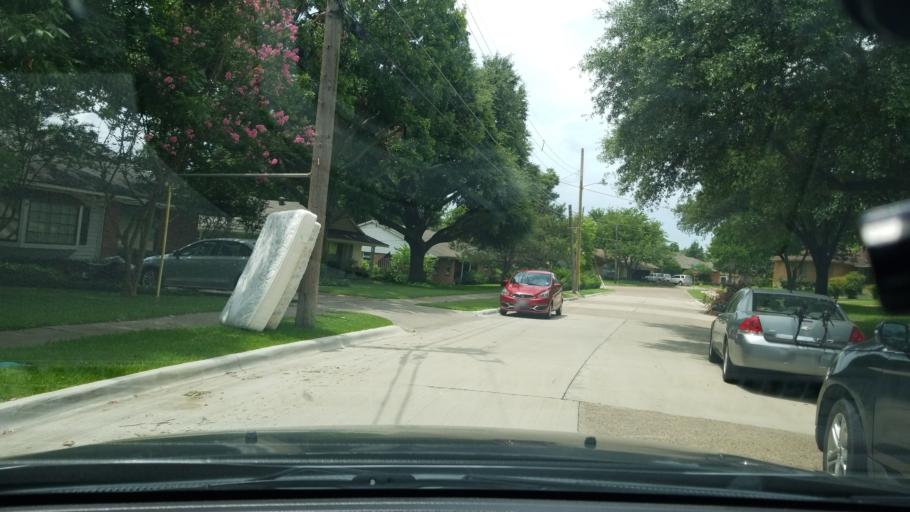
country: US
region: Texas
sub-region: Dallas County
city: Garland
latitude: 32.8255
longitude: -96.6820
